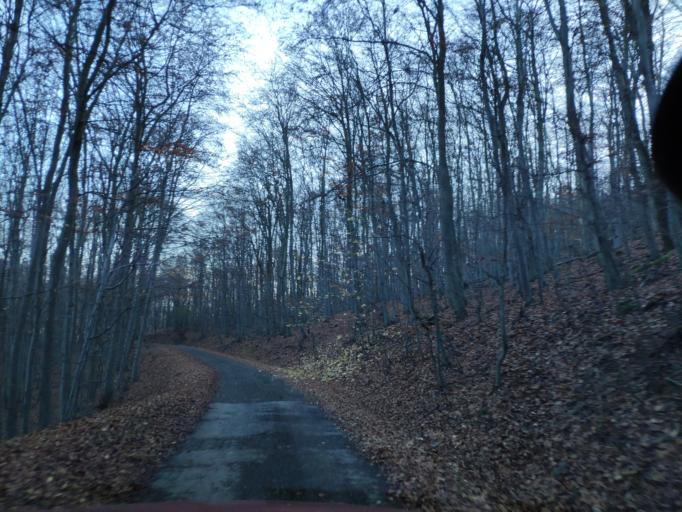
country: SK
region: Kosicky
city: Secovce
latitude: 48.5828
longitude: 21.5069
